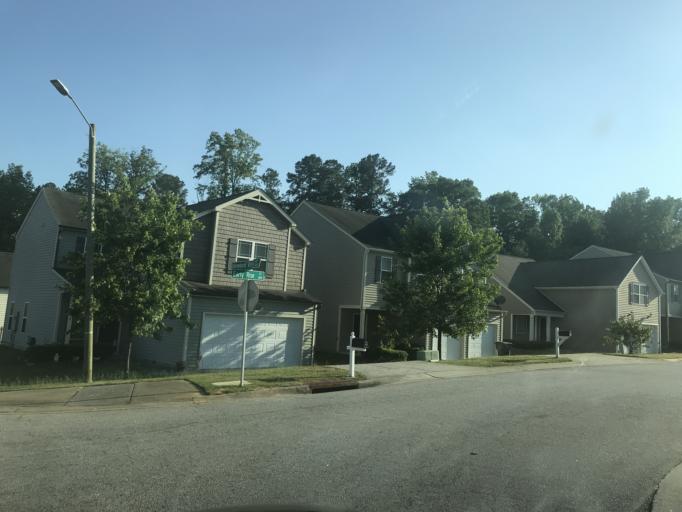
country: US
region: North Carolina
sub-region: Wake County
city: Garner
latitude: 35.7329
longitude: -78.6181
